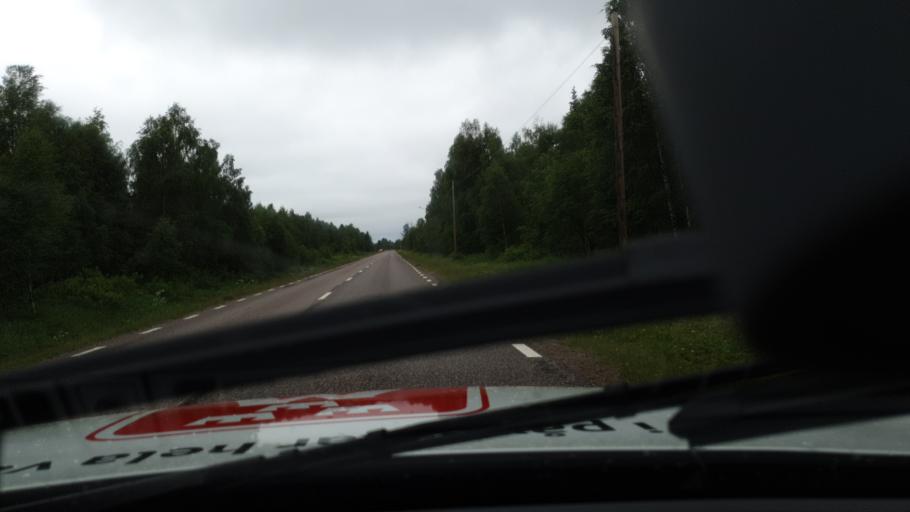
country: FI
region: Lapland
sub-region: Torniolaakso
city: Pello
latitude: 66.9351
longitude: 23.8508
